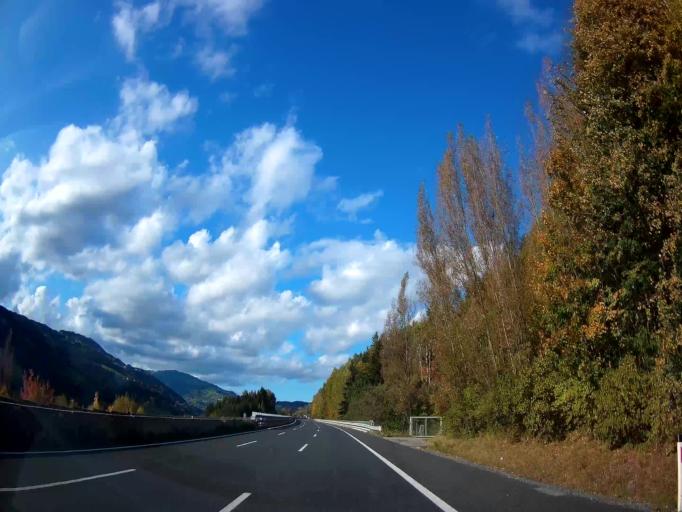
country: AT
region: Carinthia
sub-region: Politischer Bezirk Wolfsberg
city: Wolfsberg
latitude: 46.8687
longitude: 14.8361
